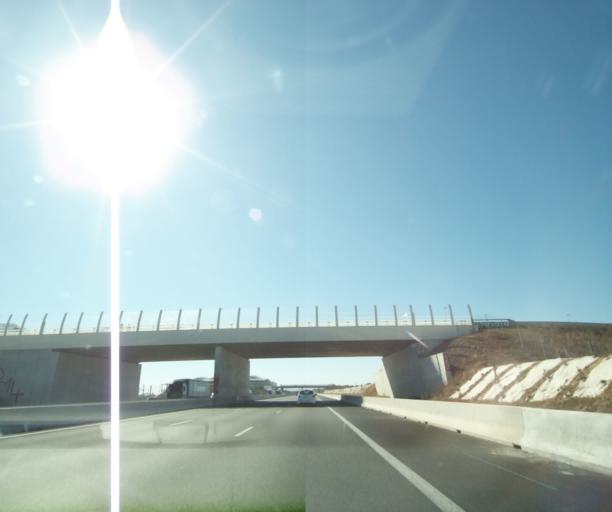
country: FR
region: Languedoc-Roussillon
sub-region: Departement de l'Herault
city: Lattes
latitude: 43.5980
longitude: 3.9283
